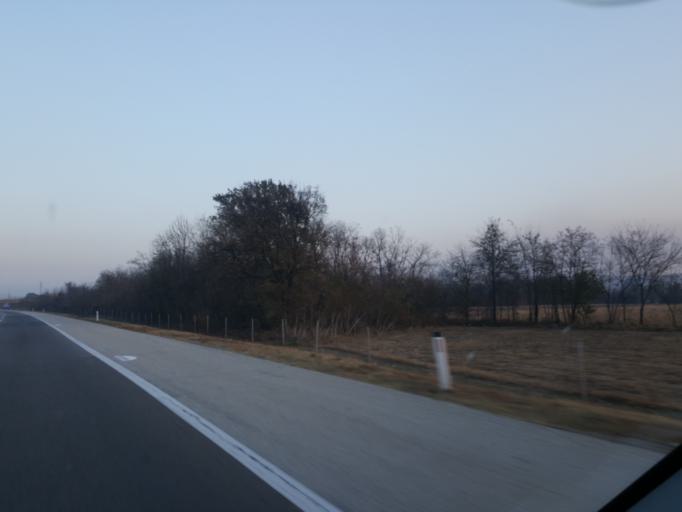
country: RS
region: Central Serbia
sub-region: Pomoravski Okrug
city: Jagodina
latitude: 43.9695
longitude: 21.3032
